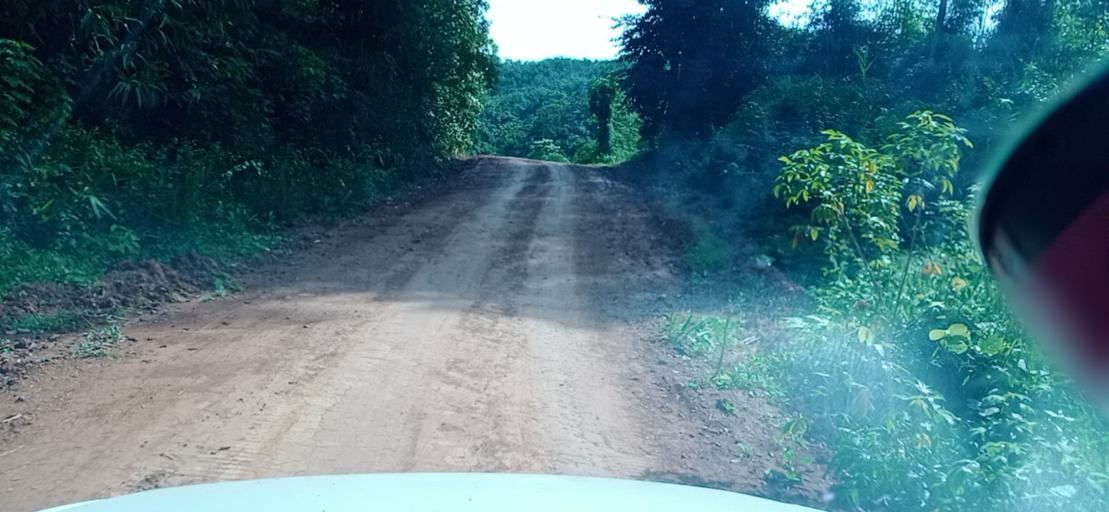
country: TH
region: Changwat Bueng Kan
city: Pak Khat
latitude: 18.6380
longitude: 103.2574
